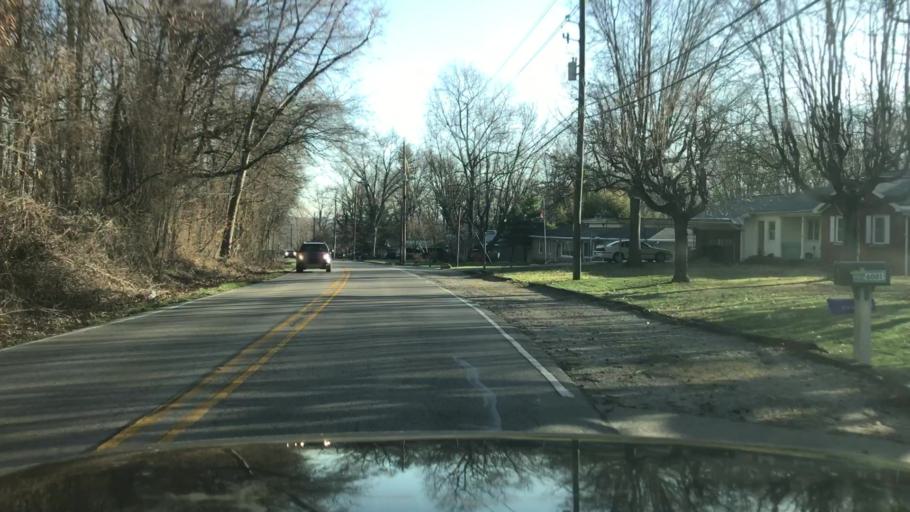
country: US
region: Indiana
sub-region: Vanderburgh County
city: Highland
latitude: 38.0343
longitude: -87.5589
